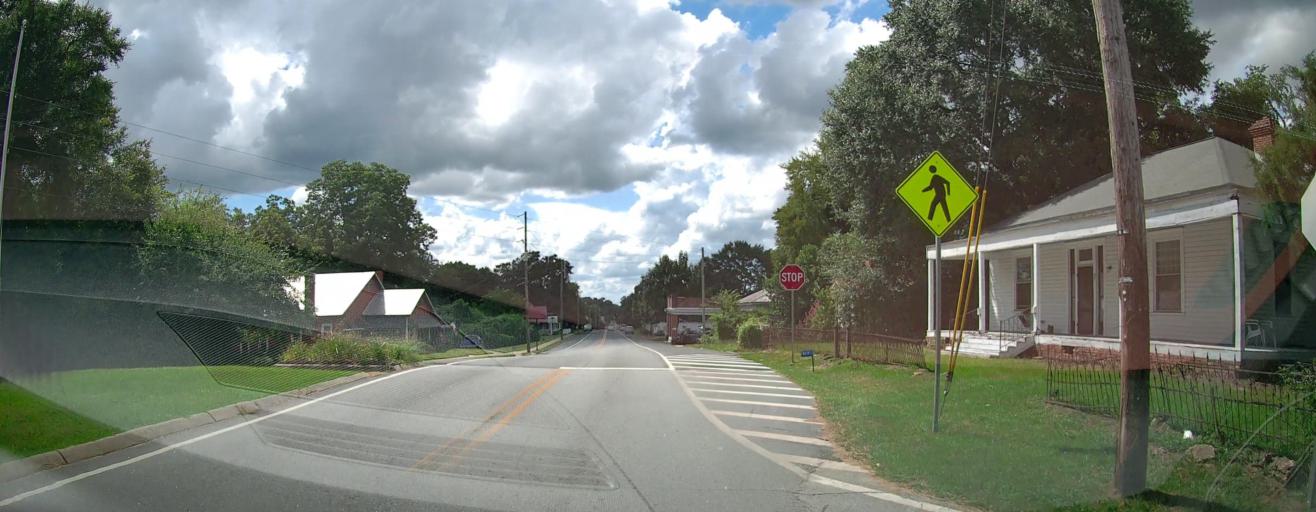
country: US
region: Georgia
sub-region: Chattahoochee County
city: Cusseta
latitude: 32.3051
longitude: -84.7731
